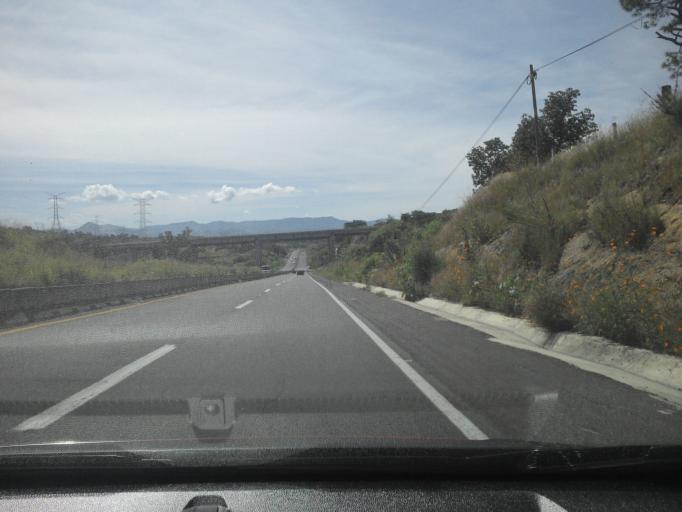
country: MX
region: Jalisco
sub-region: Tala
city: Los Ruisenores
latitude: 20.6932
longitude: -103.6914
